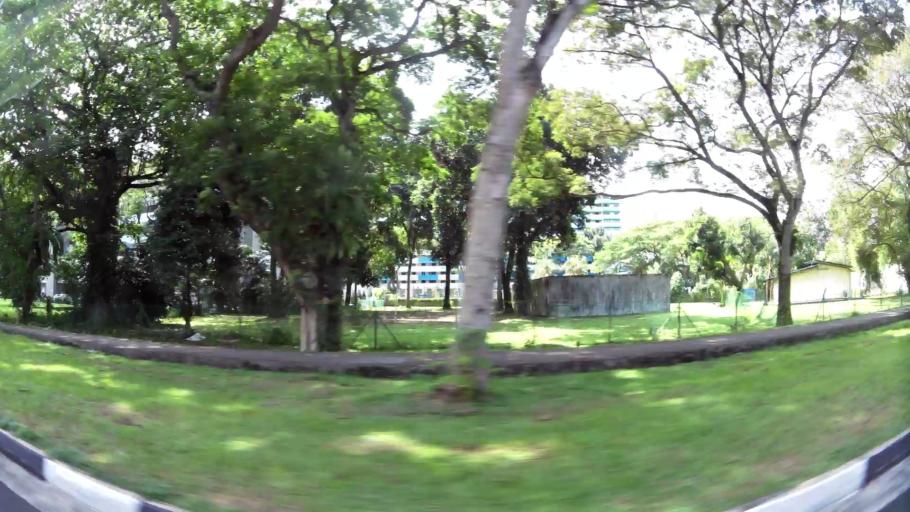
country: SG
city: Singapore
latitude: 1.3437
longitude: 103.8451
